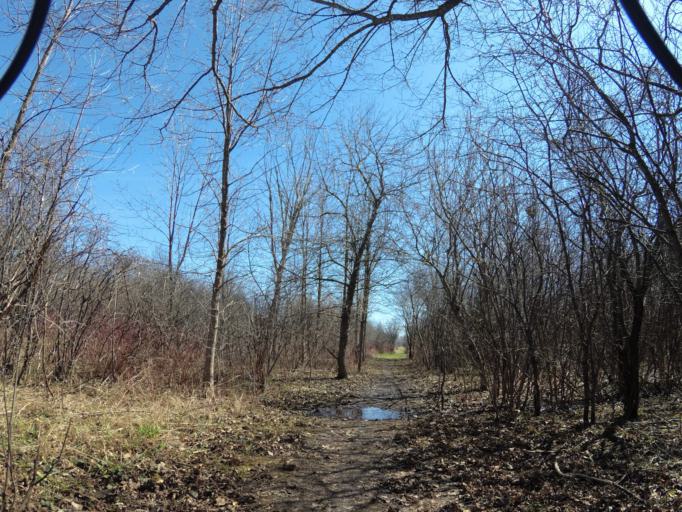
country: CA
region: Ontario
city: Ottawa
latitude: 45.3390
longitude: -75.7382
